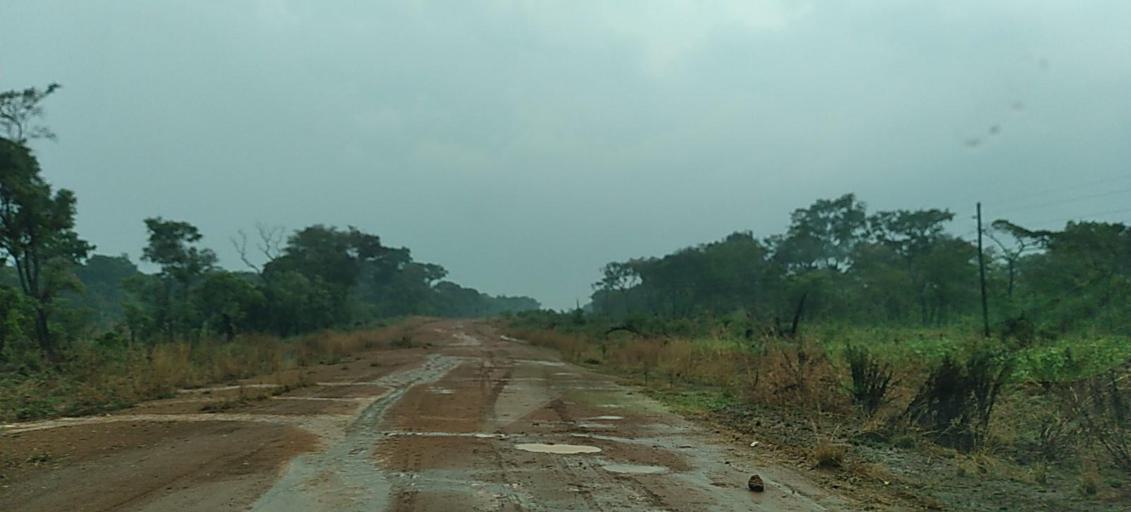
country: ZM
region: North-Western
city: Mwinilunga
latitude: -11.5970
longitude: 24.3914
